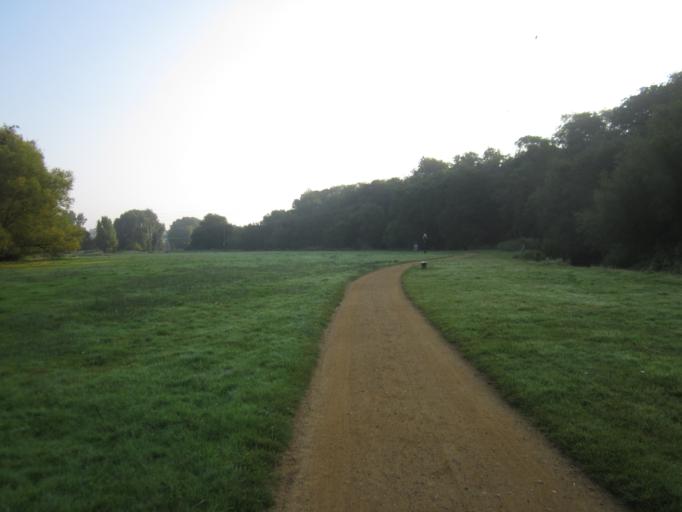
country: GB
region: England
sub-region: Kent
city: Chartham
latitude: 51.2668
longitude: 1.0416
